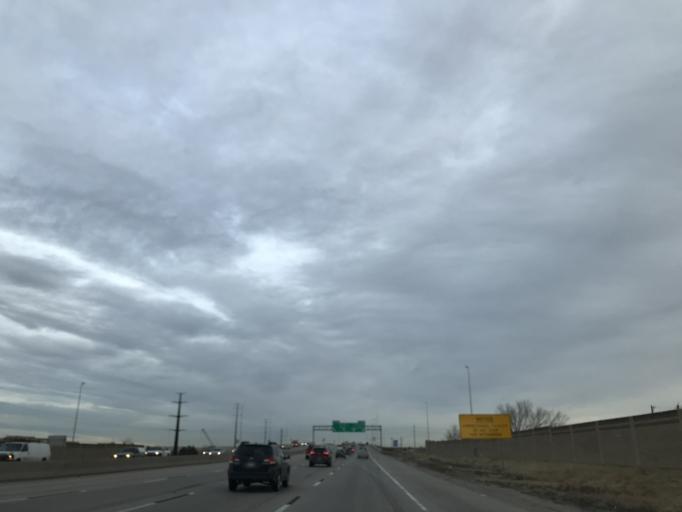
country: US
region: Colorado
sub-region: Adams County
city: Aurora
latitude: 39.7602
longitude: -104.8275
